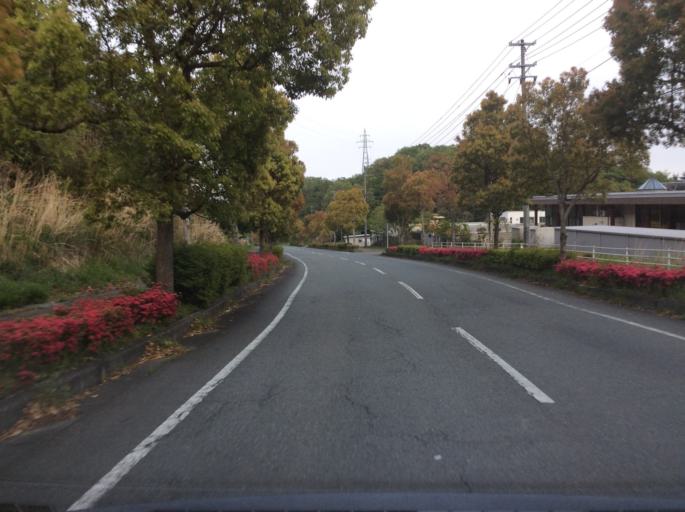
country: JP
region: Fukushima
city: Iwaki
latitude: 37.0708
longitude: 140.8648
